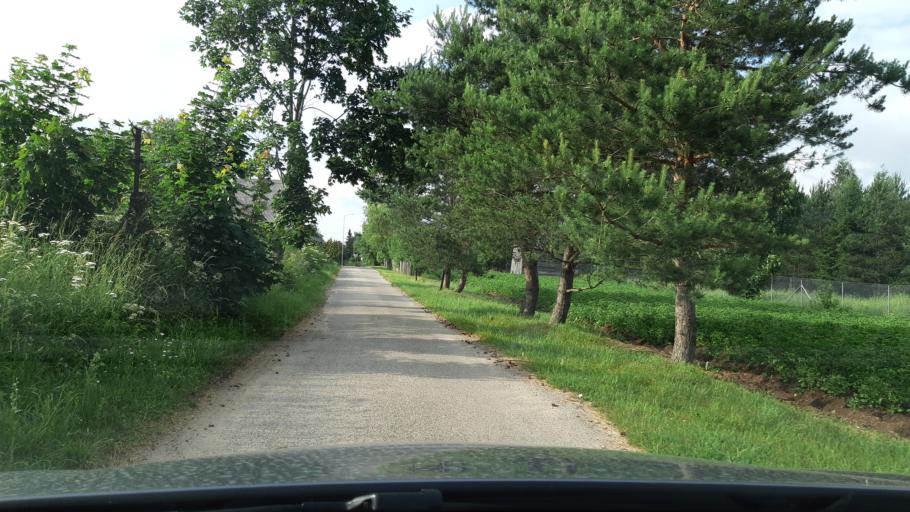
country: LT
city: Kybartai
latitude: 54.4532
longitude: 22.7204
